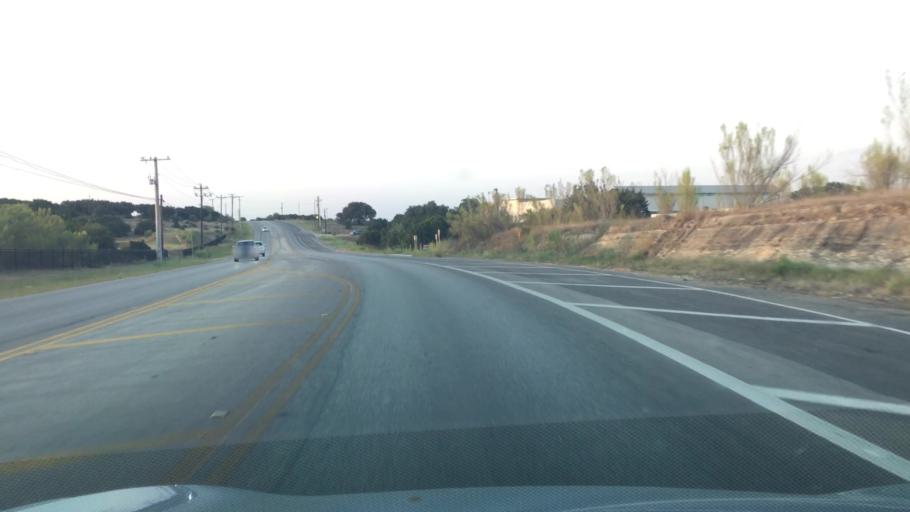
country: US
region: Texas
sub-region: Hays County
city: Dripping Springs
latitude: 30.1765
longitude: -98.0030
